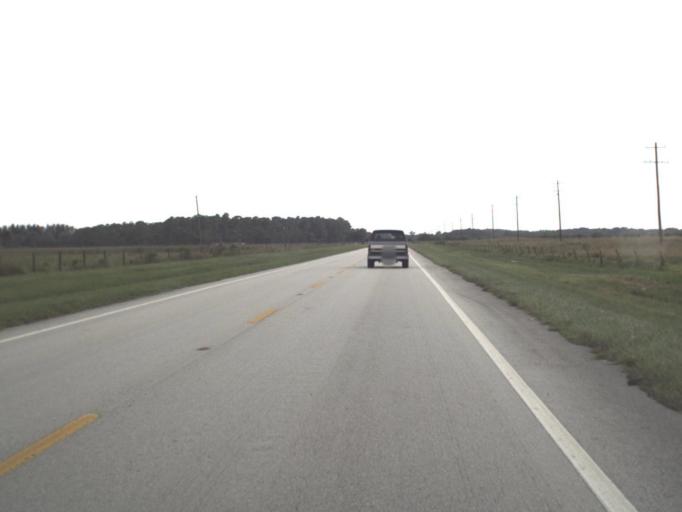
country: US
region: Florida
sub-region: Okeechobee County
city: Cypress Quarters
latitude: 27.3184
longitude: -80.8250
